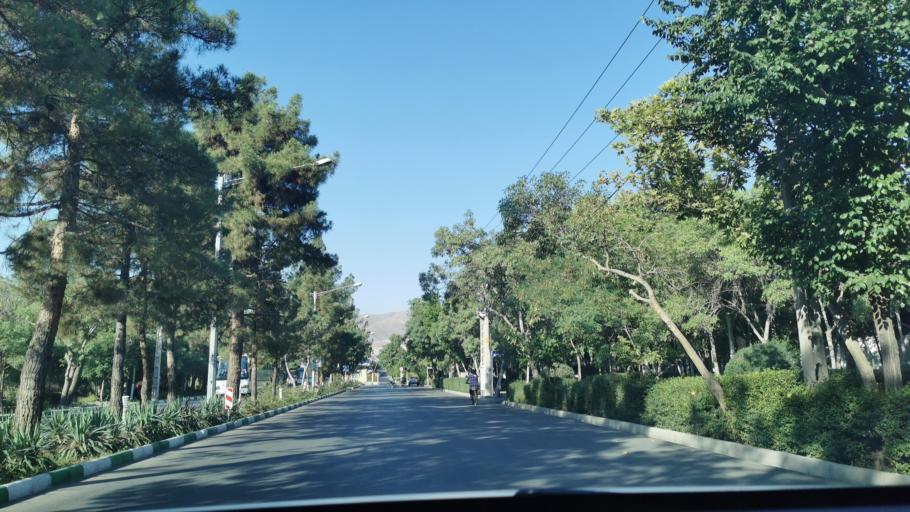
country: IR
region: Razavi Khorasan
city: Mashhad
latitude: 36.3132
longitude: 59.5234
